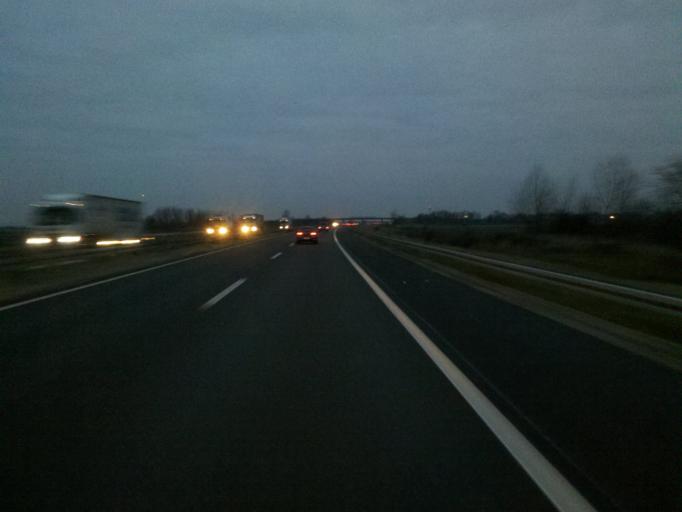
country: HR
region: Zagrebacka
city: Micevec
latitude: 45.7513
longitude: 16.0709
